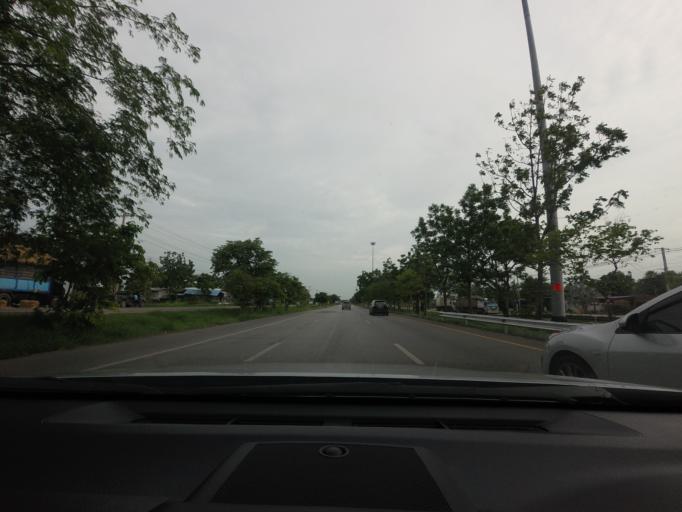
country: TH
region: Phetchaburi
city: Cha-am
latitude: 12.8052
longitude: 99.9429
